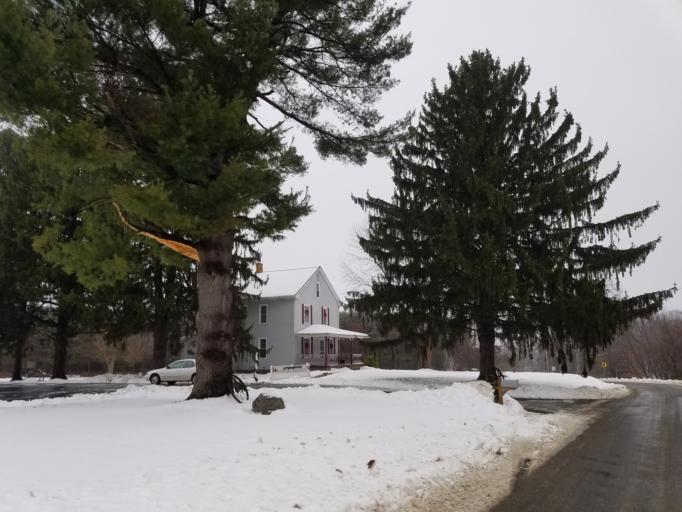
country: US
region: Pennsylvania
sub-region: Mercer County
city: Reynolds Heights
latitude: 41.3122
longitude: -80.3539
